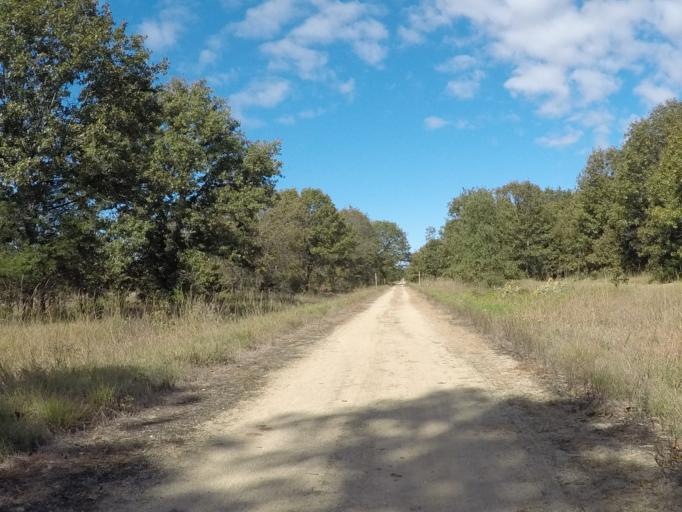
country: US
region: Wisconsin
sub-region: Sauk County
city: Spring Green
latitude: 43.1884
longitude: -90.2172
